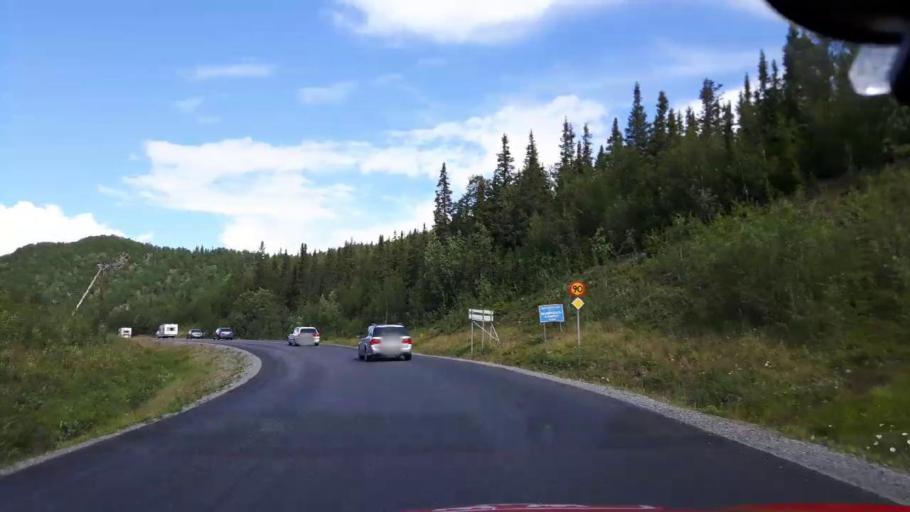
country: SE
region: Vaesterbotten
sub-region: Vilhelmina Kommun
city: Sjoberg
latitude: 65.0329
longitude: 15.1406
